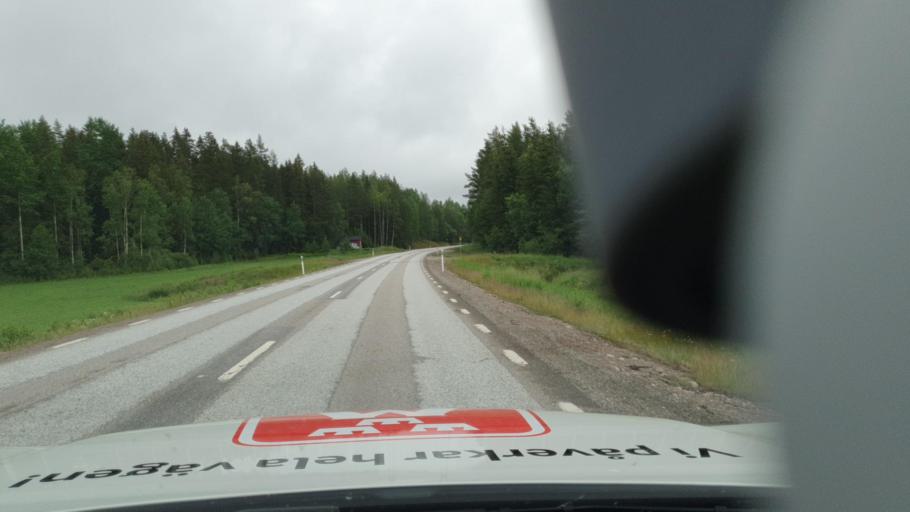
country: SE
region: Vaermland
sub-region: Kristinehamns Kommun
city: Bjorneborg
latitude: 59.2526
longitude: 14.1957
